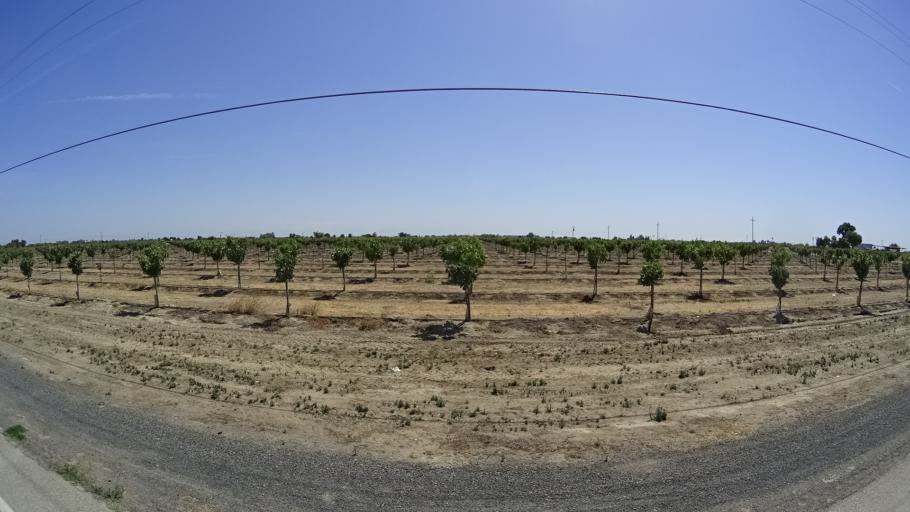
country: US
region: California
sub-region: Kings County
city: Lemoore
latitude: 36.2518
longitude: -119.7809
